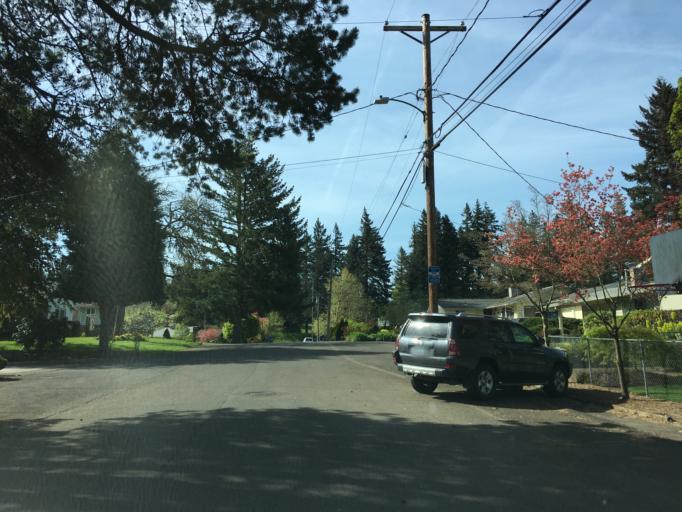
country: US
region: Oregon
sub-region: Multnomah County
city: Lents
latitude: 45.5351
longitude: -122.5156
